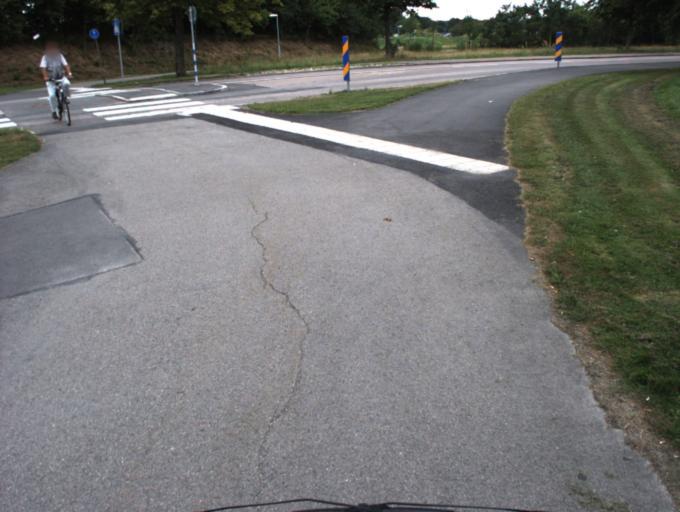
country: SE
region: Skane
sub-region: Helsingborg
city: Helsingborg
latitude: 56.0510
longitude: 12.7345
